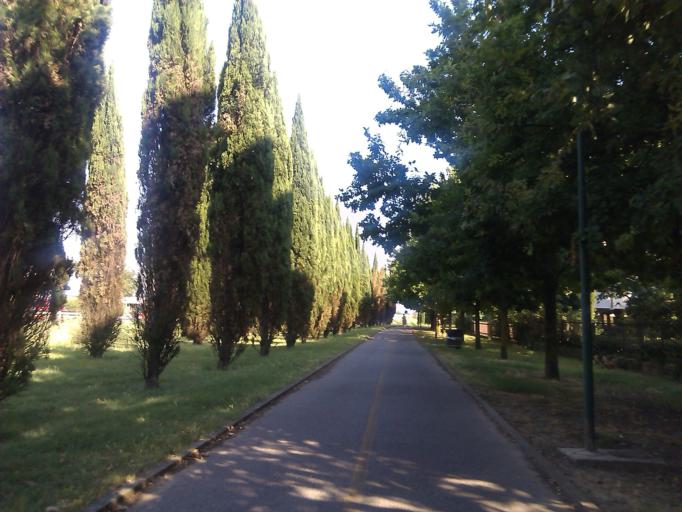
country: IT
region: Tuscany
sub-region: Province of Florence
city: Campi Bisenzio
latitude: 43.8238
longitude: 11.1457
